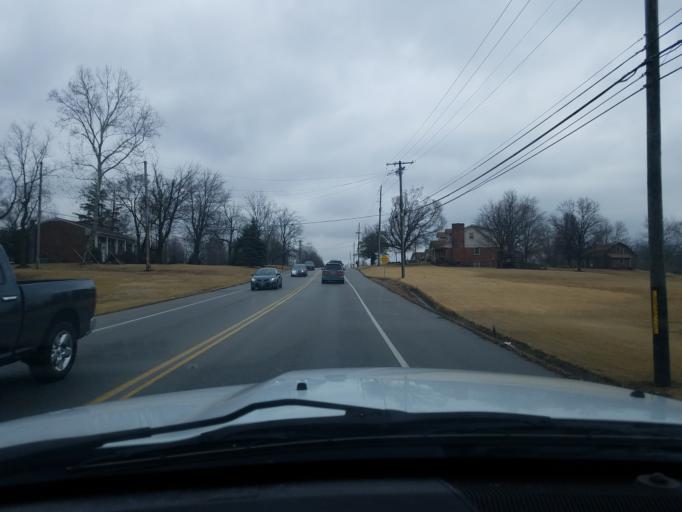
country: US
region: Indiana
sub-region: Clark County
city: Oak Park
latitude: 38.3319
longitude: -85.7299
